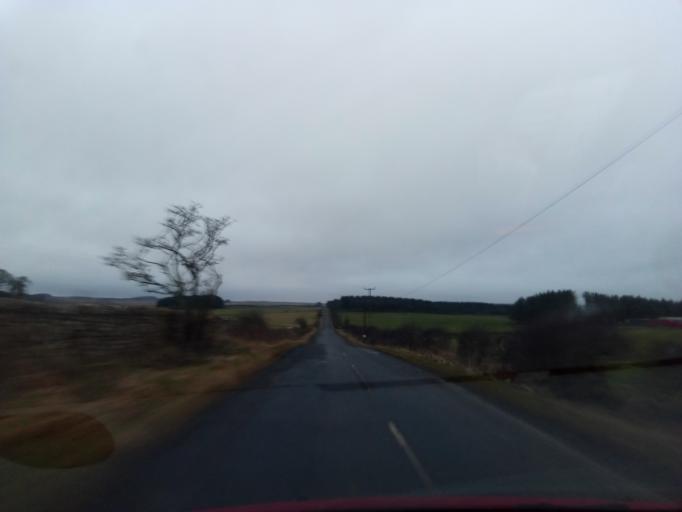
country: GB
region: England
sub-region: Northumberland
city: Rothley
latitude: 55.1994
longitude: -1.9773
